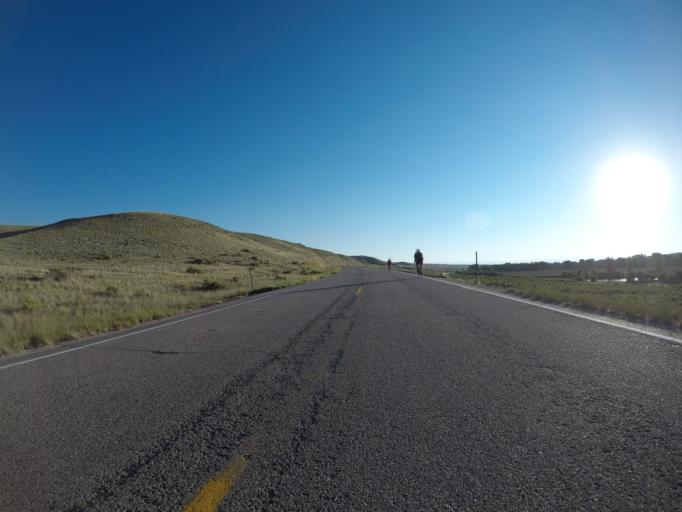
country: US
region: Wyoming
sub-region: Sublette County
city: Marbleton
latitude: 42.5806
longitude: -109.9240
